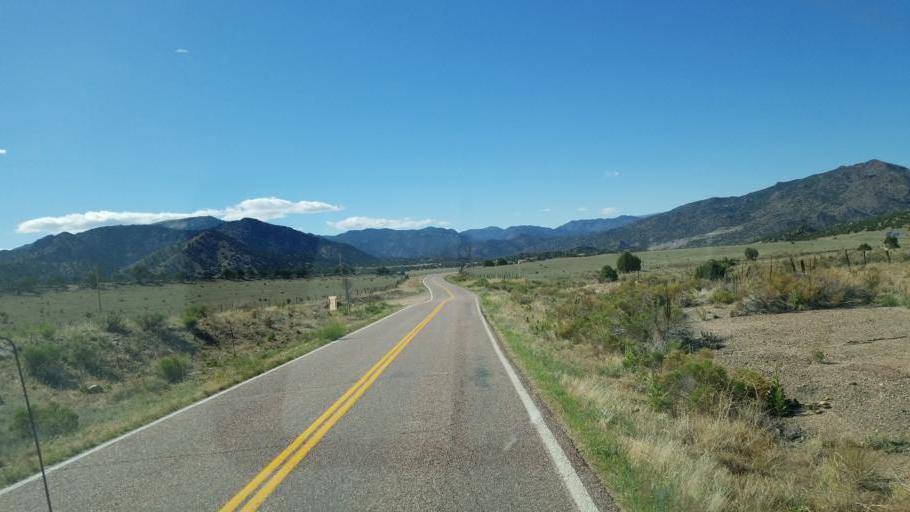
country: US
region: Colorado
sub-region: Fremont County
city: Canon City
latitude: 38.4557
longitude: -105.3736
